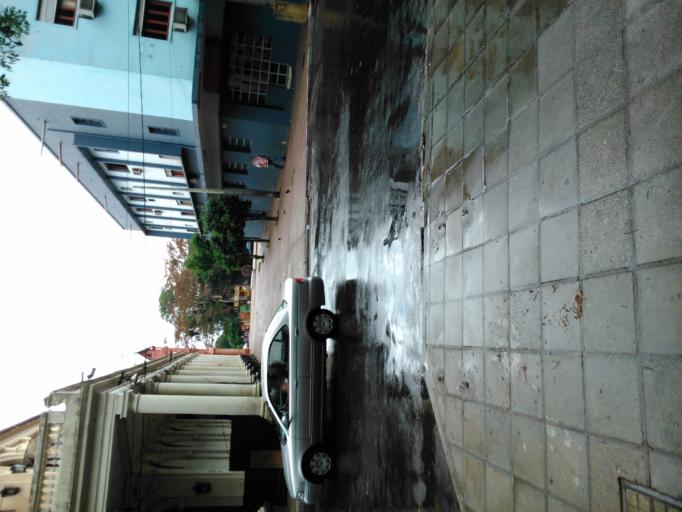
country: PY
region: Asuncion
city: Asuncion
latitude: -25.2844
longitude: -57.6296
